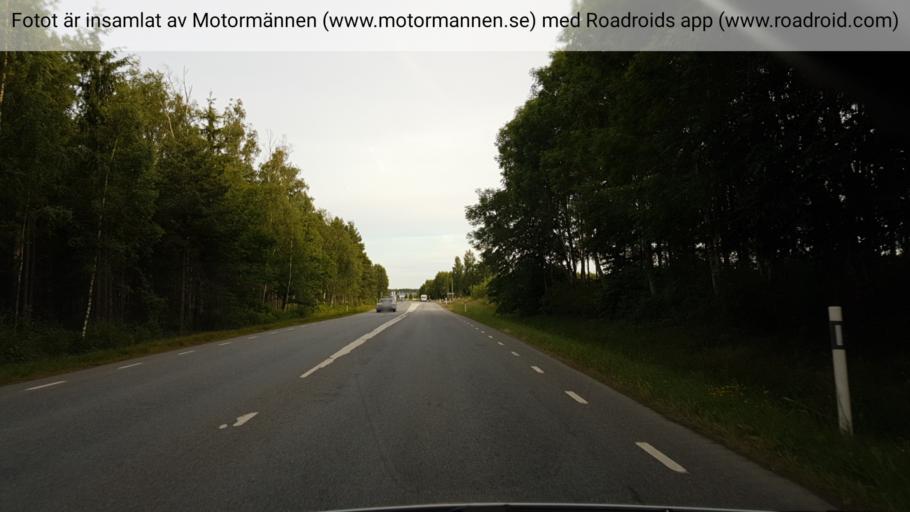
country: SE
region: Vaestra Goetaland
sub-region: Lidkopings Kommun
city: Lidkoping
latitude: 58.5127
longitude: 13.1168
